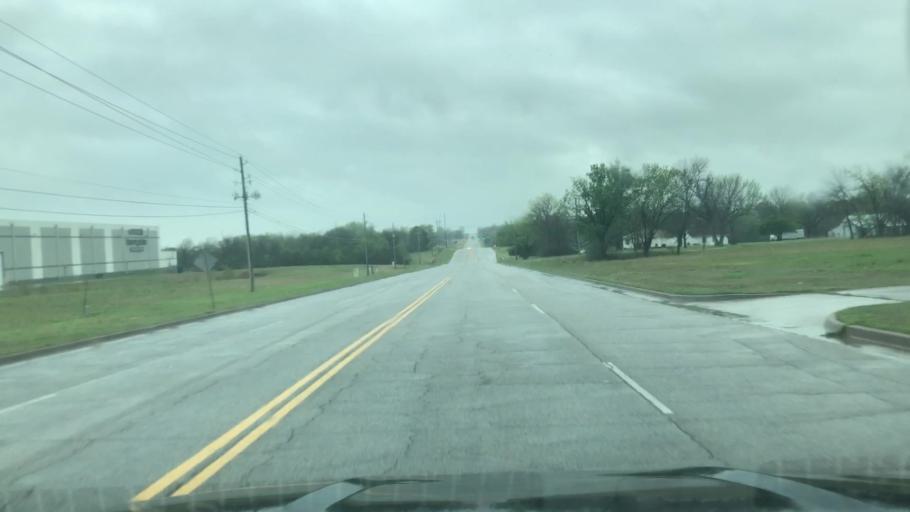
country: US
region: Oklahoma
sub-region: Tulsa County
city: Owasso
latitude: 36.2640
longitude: -95.8961
